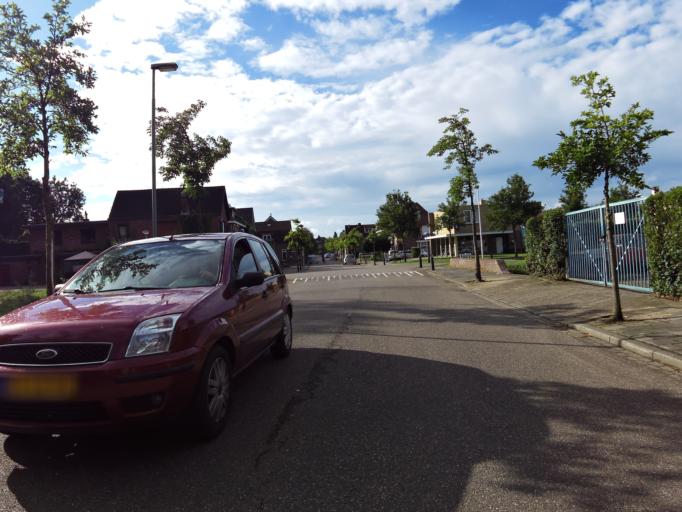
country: NL
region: Limburg
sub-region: Gemeente Heerlen
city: Nieuw-Lotbroek
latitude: 50.9175
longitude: 5.9242
